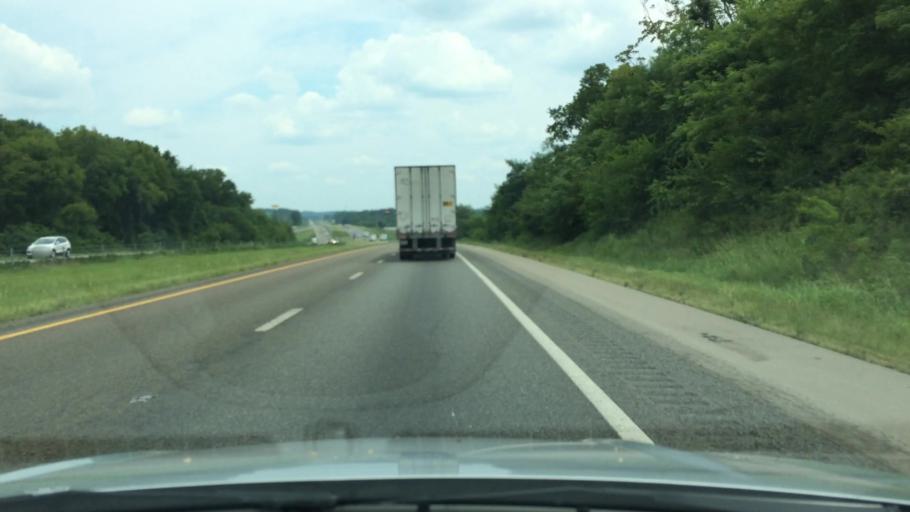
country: US
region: Tennessee
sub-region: Maury County
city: Spring Hill
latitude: 35.6362
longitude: -86.8945
